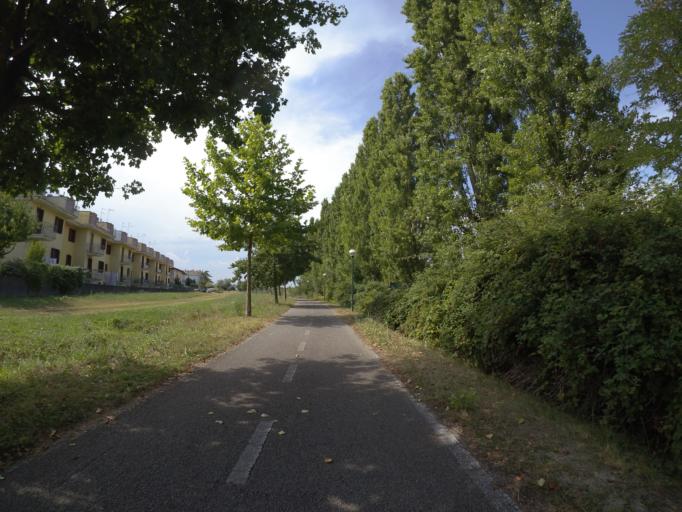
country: IT
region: Friuli Venezia Giulia
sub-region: Provincia di Udine
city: Lignano Sabbiadoro
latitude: 45.6639
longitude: 13.0743
